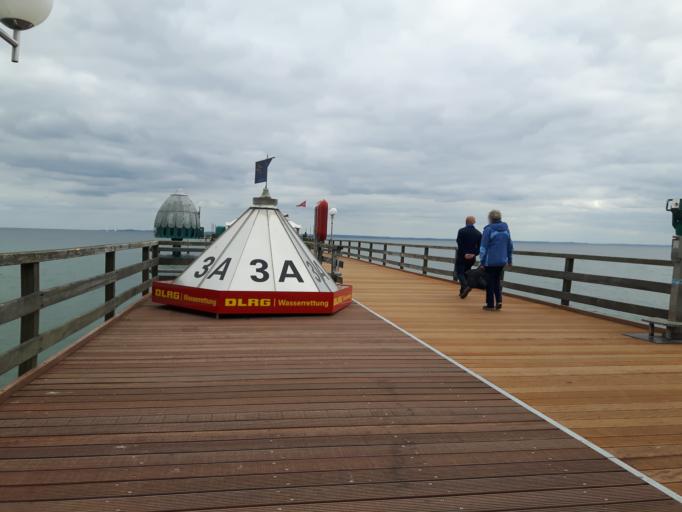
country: DE
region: Schleswig-Holstein
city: Gromitz
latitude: 54.1421
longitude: 10.9648
